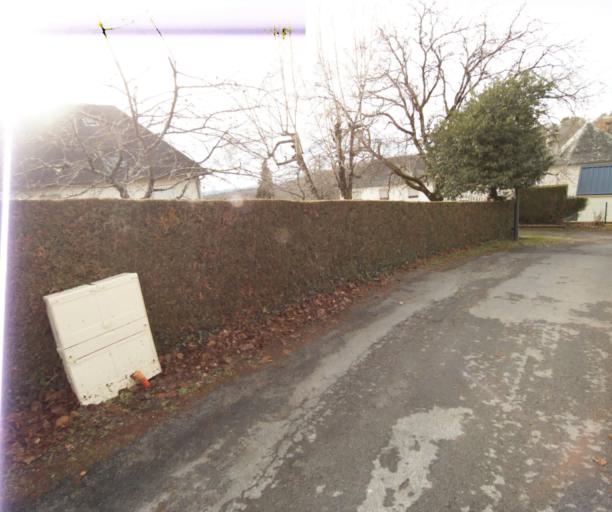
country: FR
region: Limousin
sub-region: Departement de la Correze
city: Saint-Mexant
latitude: 45.2639
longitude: 1.6776
